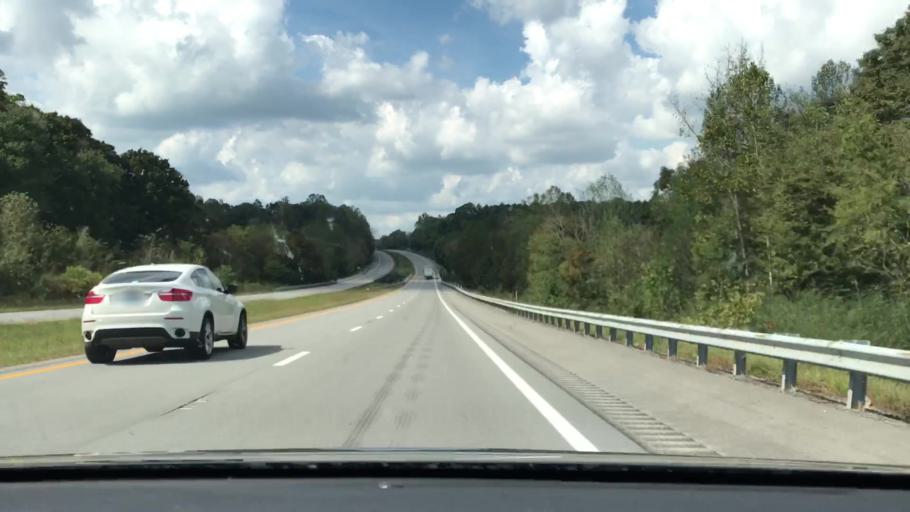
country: US
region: Kentucky
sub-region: Russell County
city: Russell Springs
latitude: 37.0587
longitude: -85.1751
